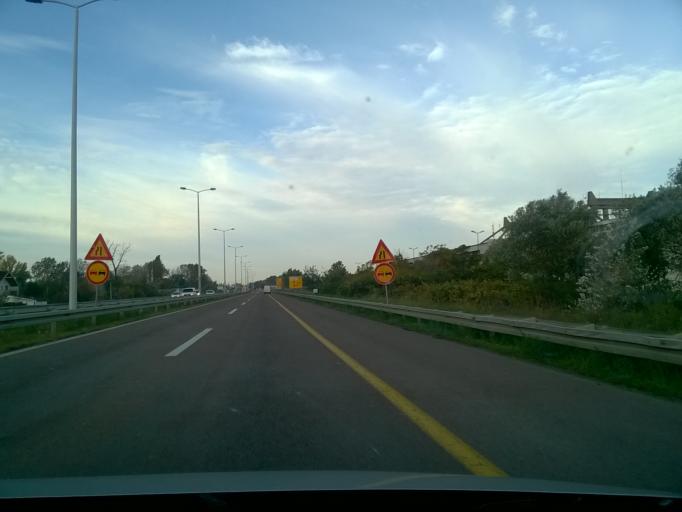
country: RS
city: Ovca
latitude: 44.8489
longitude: 20.5230
